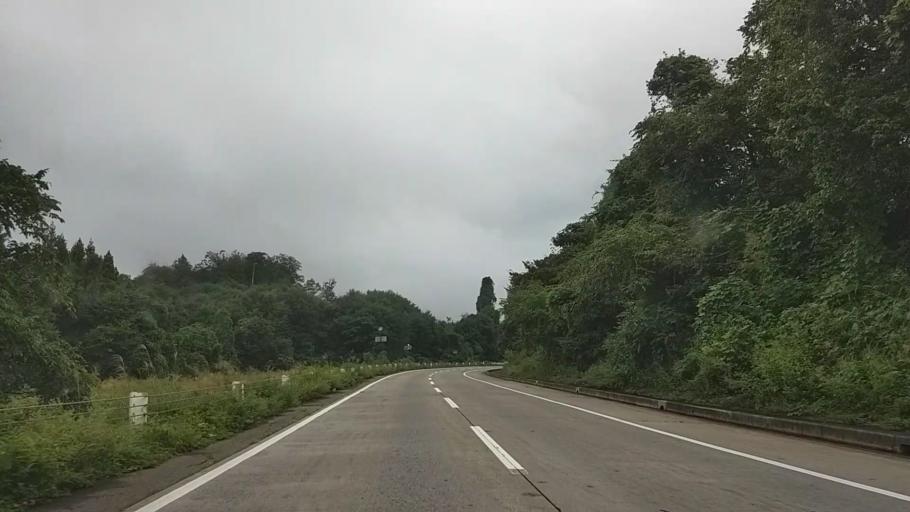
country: JP
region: Nagano
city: Iiyama
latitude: 36.8156
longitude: 138.3437
